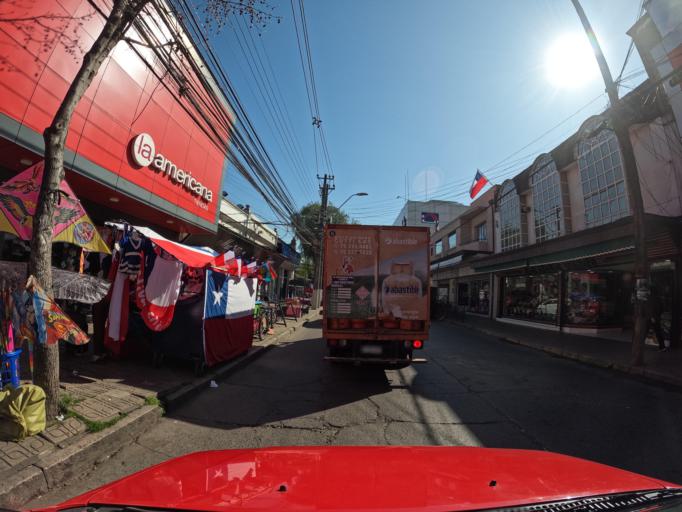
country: CL
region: Maule
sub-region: Provincia de Curico
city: Curico
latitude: -34.9830
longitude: -71.2417
